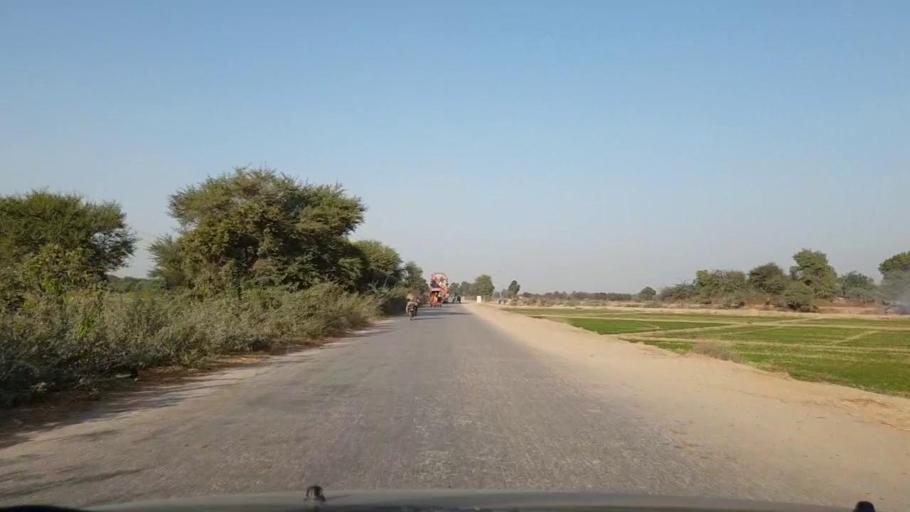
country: PK
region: Sindh
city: Chambar
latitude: 25.2225
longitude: 68.7822
